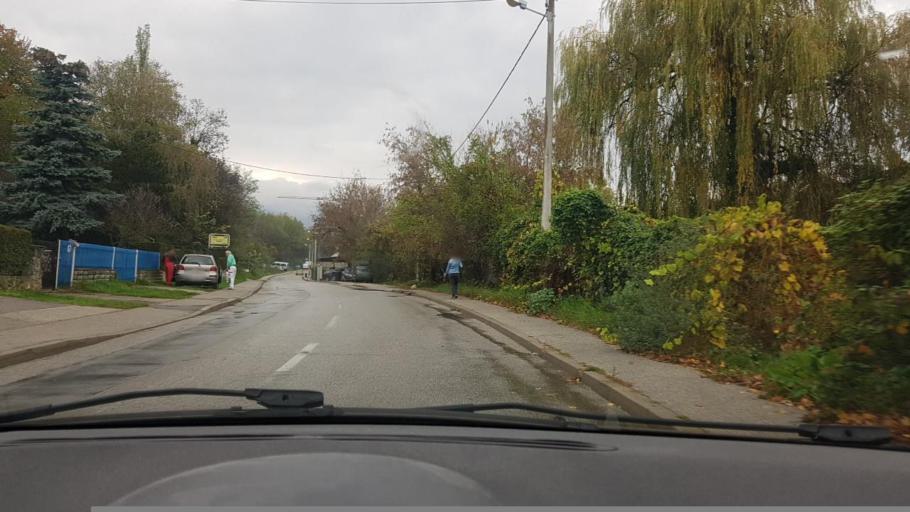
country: HR
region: Grad Zagreb
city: Zagreb
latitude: 45.8286
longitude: 16.0063
